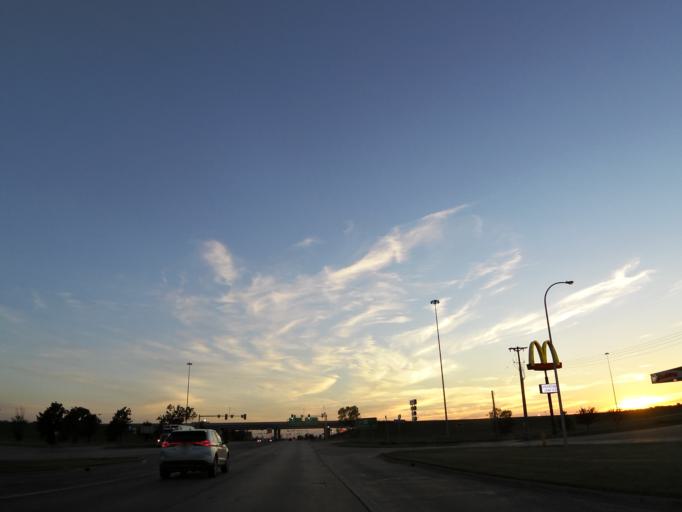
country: US
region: North Dakota
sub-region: Grand Forks County
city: Grand Forks
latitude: 47.9331
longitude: -97.0906
